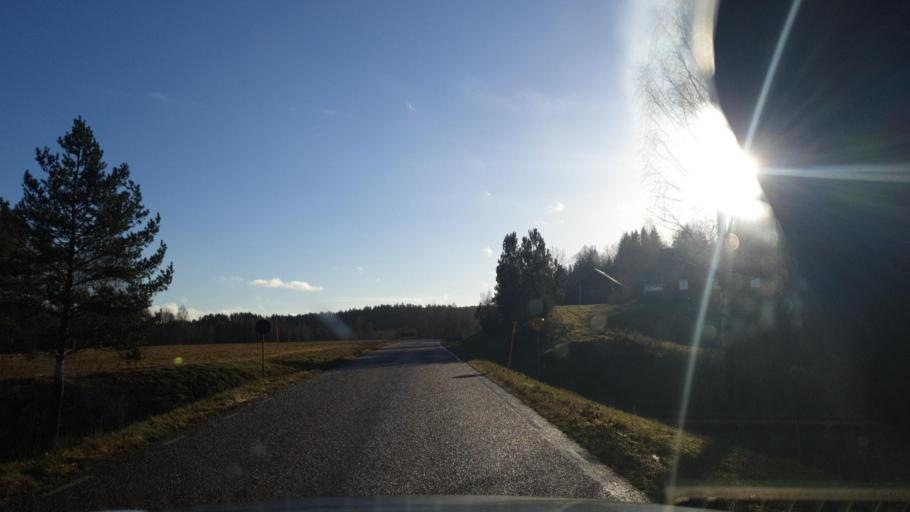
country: NO
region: Ostfold
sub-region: Romskog
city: Romskog
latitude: 59.8061
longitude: 12.0078
